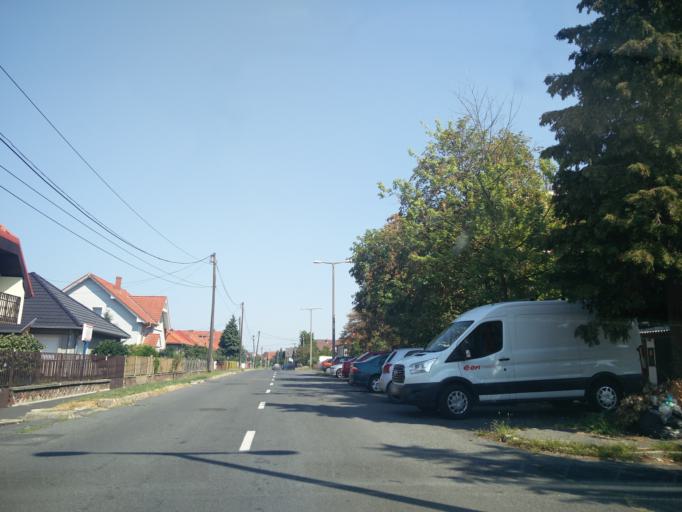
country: HU
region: Zala
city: Zalaegerszeg
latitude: 46.8271
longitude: 16.8302
